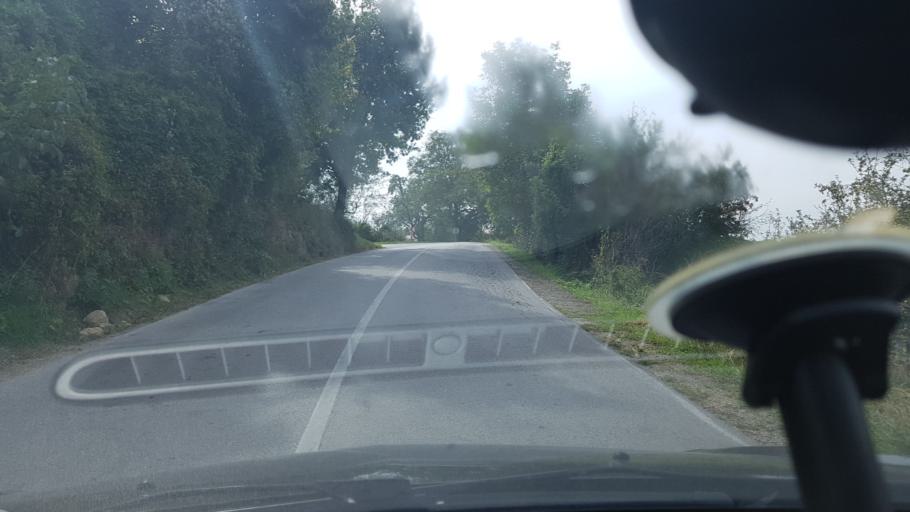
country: HR
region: Varazdinska
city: Ljubescica
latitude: 46.0937
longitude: 16.3341
